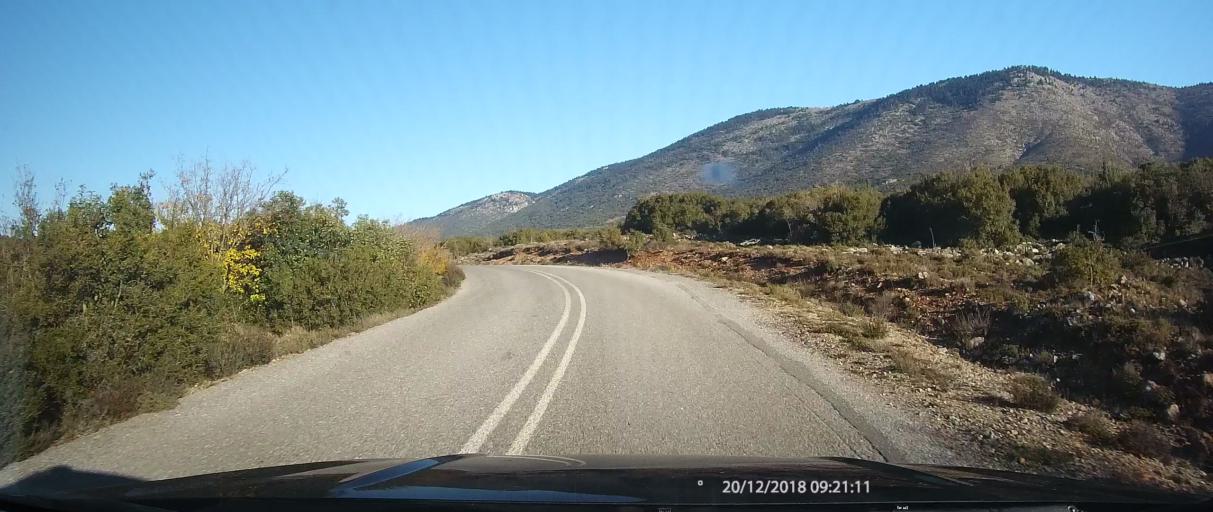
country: GR
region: Peloponnese
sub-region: Nomos Lakonias
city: Molaoi
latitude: 36.9377
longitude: 22.9163
